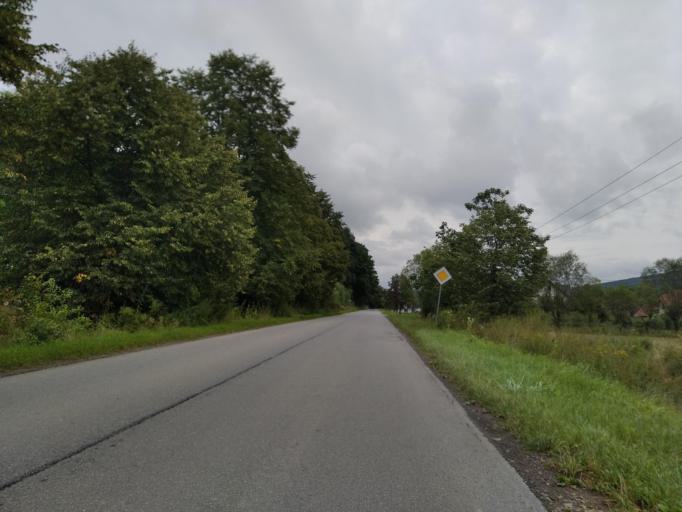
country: PL
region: Subcarpathian Voivodeship
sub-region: Powiat przemyski
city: Bircza
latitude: 49.6881
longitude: 22.3970
